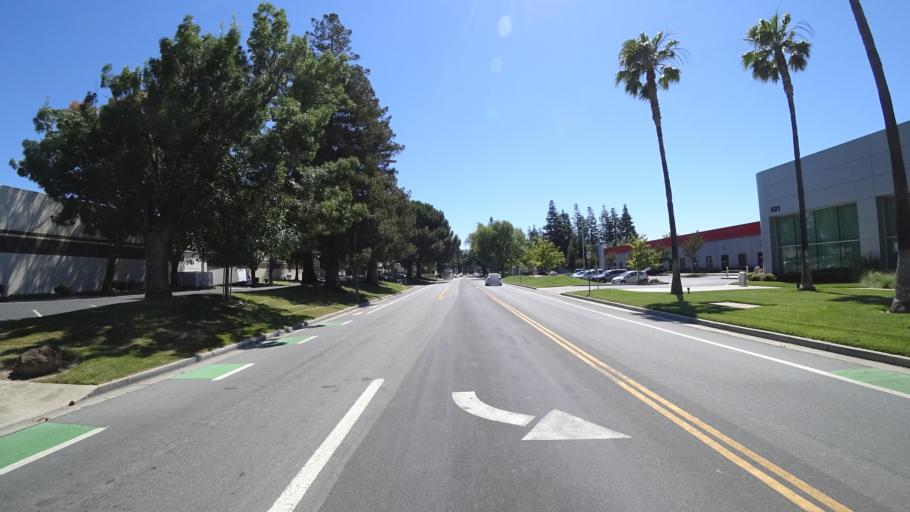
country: US
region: California
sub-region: Santa Clara County
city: Milpitas
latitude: 37.3839
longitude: -121.9133
